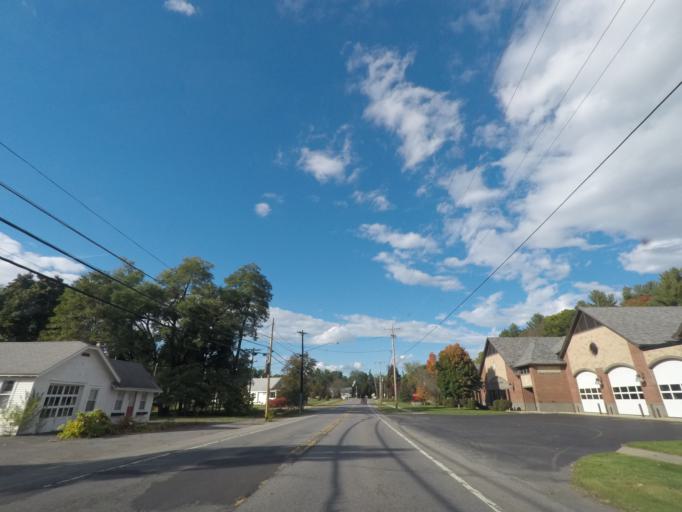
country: US
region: New York
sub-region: Schenectady County
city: Rotterdam
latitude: 42.7396
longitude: -73.9418
